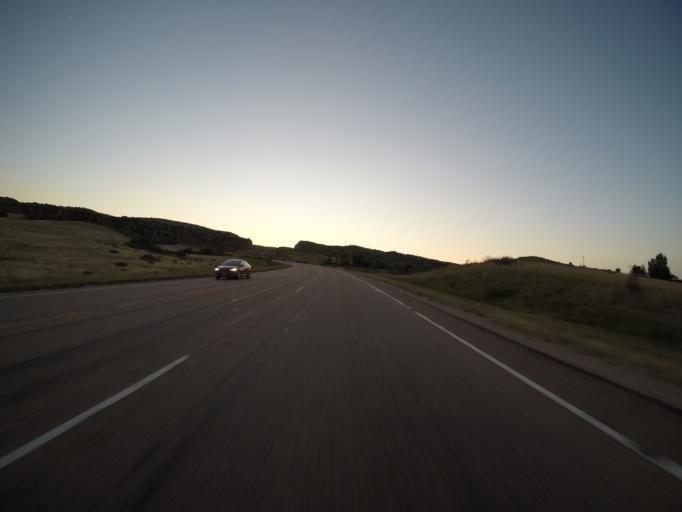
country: US
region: Colorado
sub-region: Larimer County
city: Laporte
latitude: 40.7601
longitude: -105.1739
